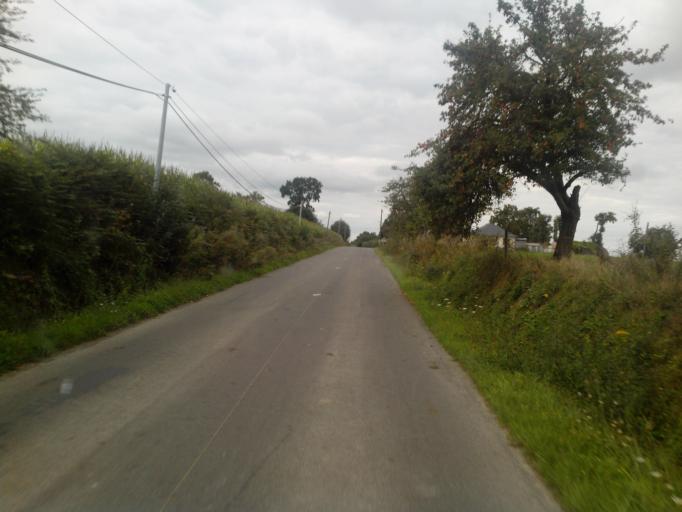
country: FR
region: Brittany
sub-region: Departement d'Ille-et-Vilaine
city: Melesse
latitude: 48.2248
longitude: -1.6897
